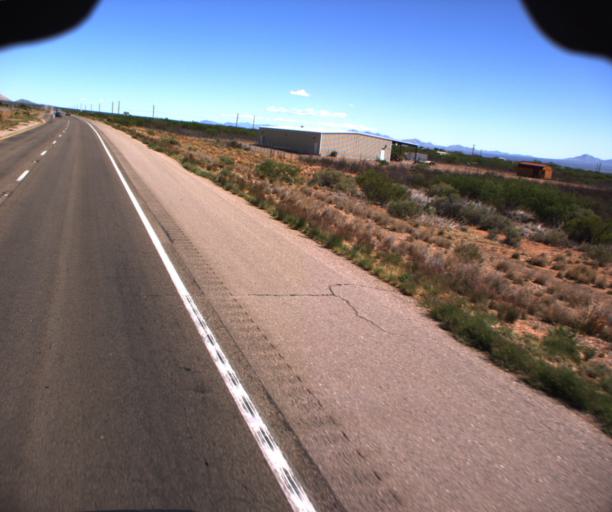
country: US
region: Arizona
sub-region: Cochise County
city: Huachuca City
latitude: 31.7243
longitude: -110.3500
